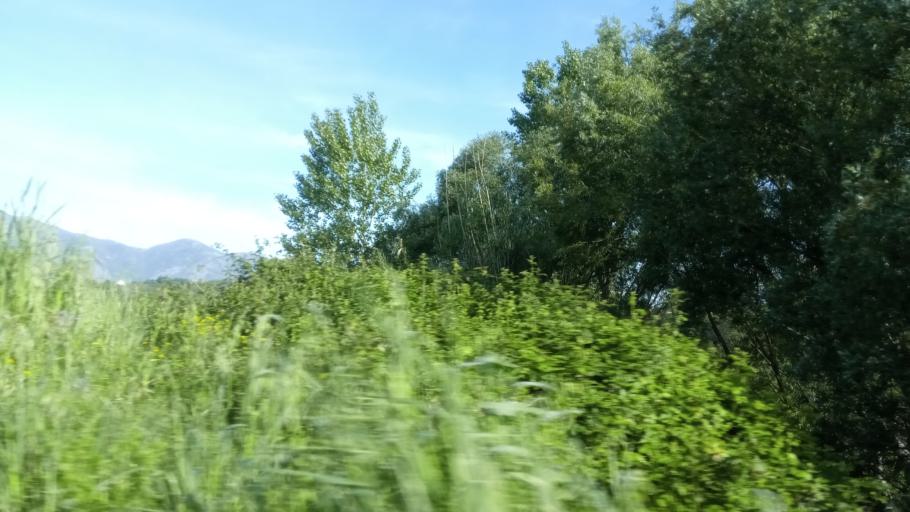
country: IT
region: Latium
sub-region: Provincia di Latina
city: Grunuovo-Campomaggiore San Luca
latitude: 41.2852
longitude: 13.7750
